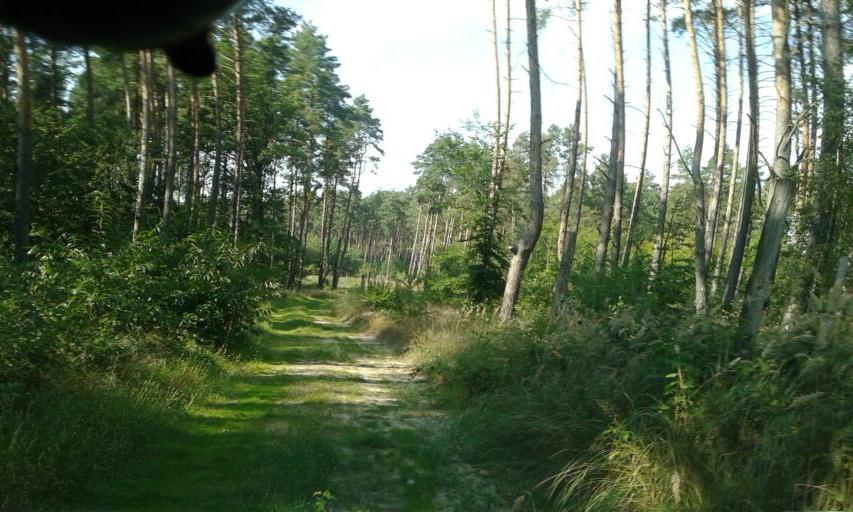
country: PL
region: West Pomeranian Voivodeship
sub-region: Powiat choszczenski
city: Krzecin
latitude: 53.0882
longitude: 15.4511
